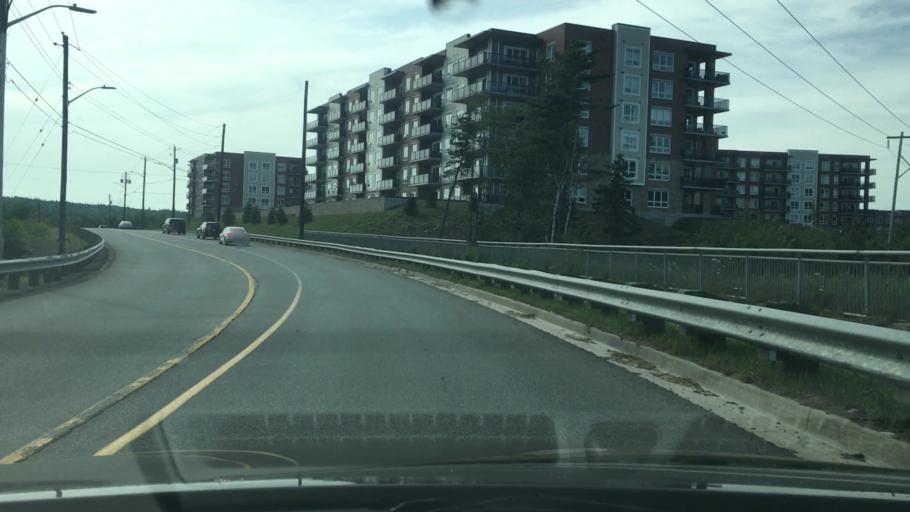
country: CA
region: Nova Scotia
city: Dartmouth
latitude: 44.6996
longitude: -63.6956
